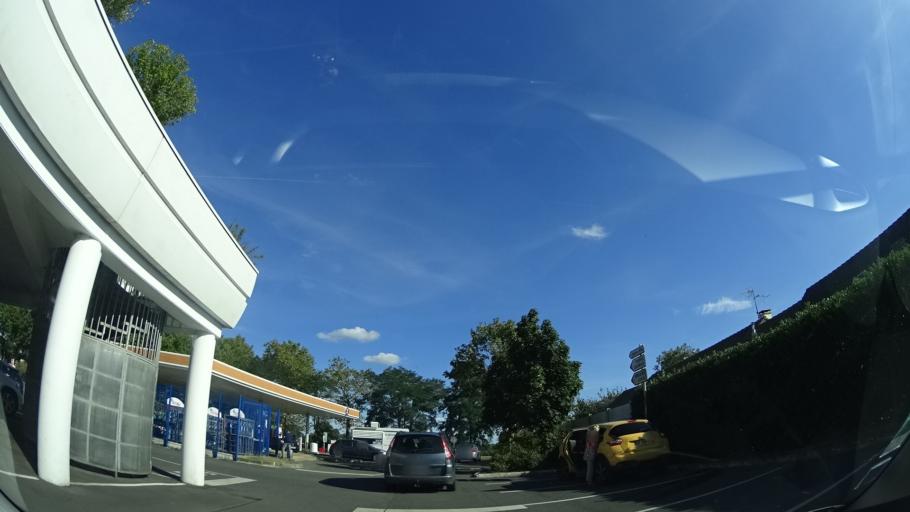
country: FR
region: Pays de la Loire
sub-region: Departement de la Sarthe
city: La Fleche
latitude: 47.7016
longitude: -0.0564
